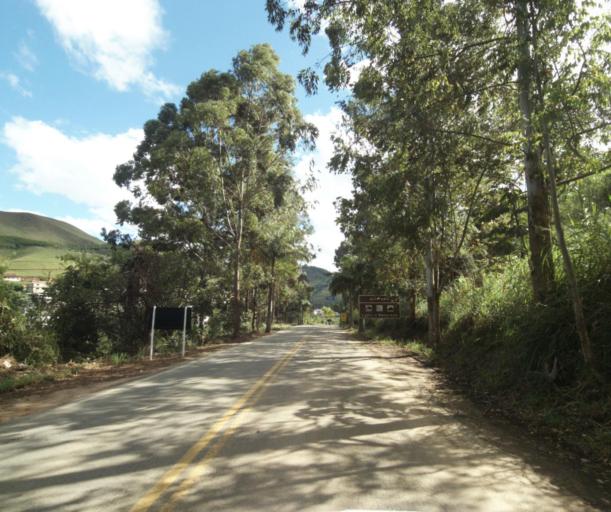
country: BR
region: Espirito Santo
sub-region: Irupi
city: Irupi
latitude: -20.5364
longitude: -41.6593
